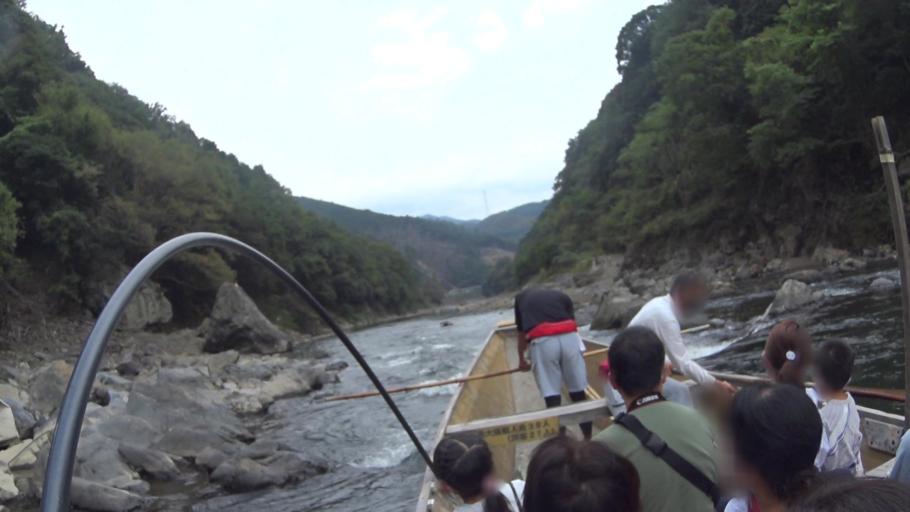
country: JP
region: Kyoto
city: Kameoka
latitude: 35.0183
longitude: 135.6107
